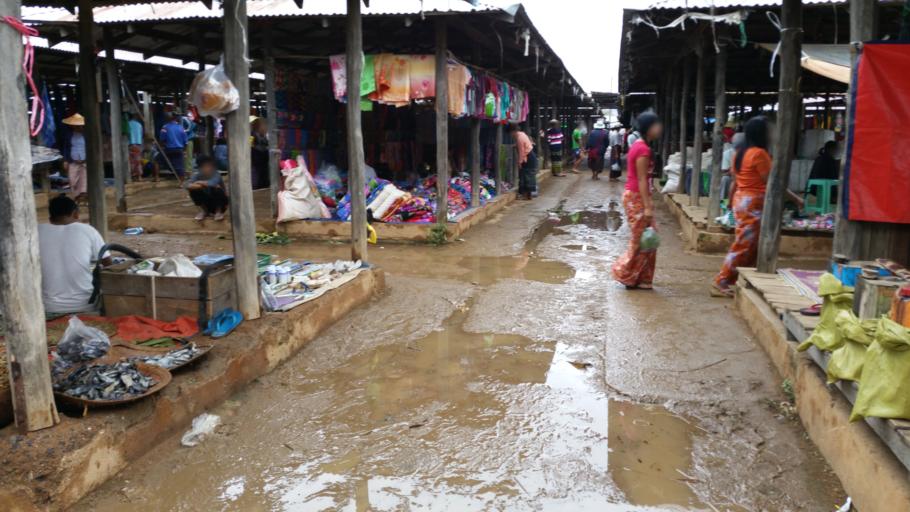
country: MM
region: Shan
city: Taunggyi
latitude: 20.4732
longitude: 96.8911
